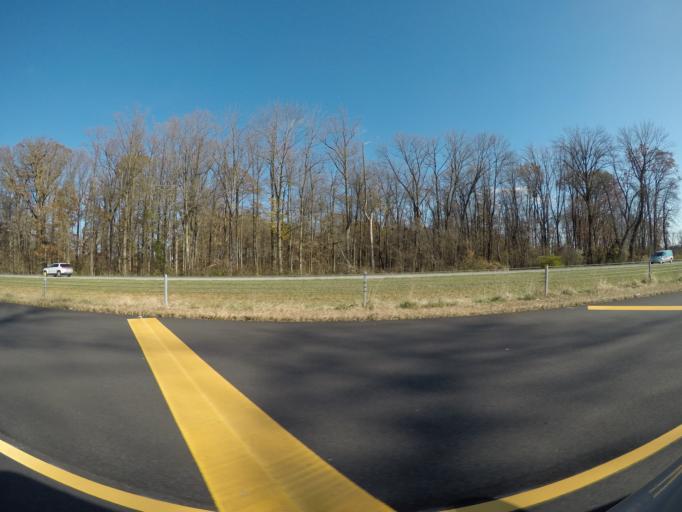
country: US
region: Maryland
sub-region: Cecil County
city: Rising Sun
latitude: 39.7270
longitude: -76.0276
